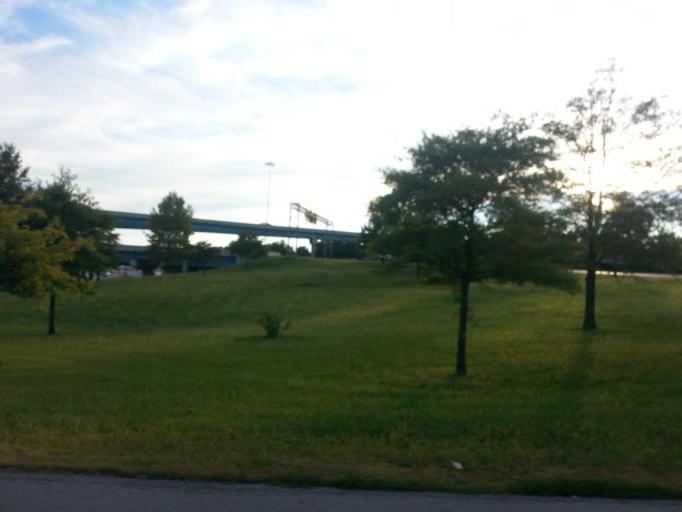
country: US
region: Tennessee
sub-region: Knox County
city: Knoxville
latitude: 35.9696
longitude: -83.9285
